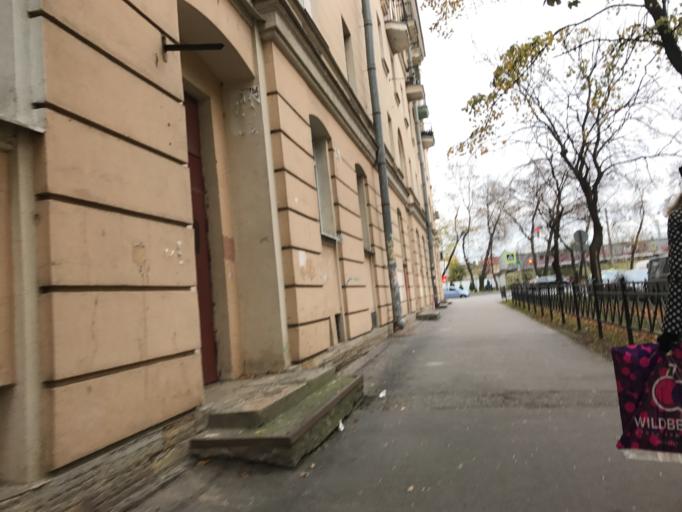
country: RU
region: St.-Petersburg
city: Obukhovo
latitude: 59.8984
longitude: 30.4294
